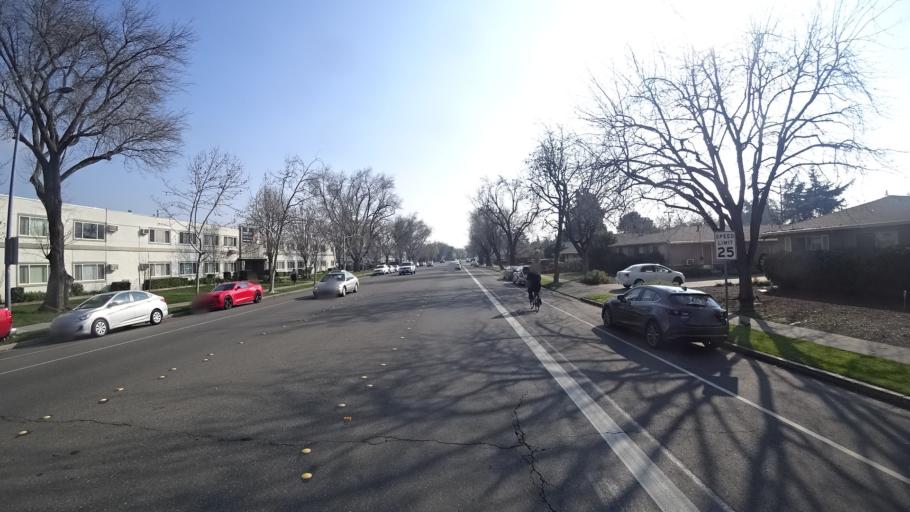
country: US
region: California
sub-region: Yolo County
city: Davis
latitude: 38.5563
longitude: -121.7432
